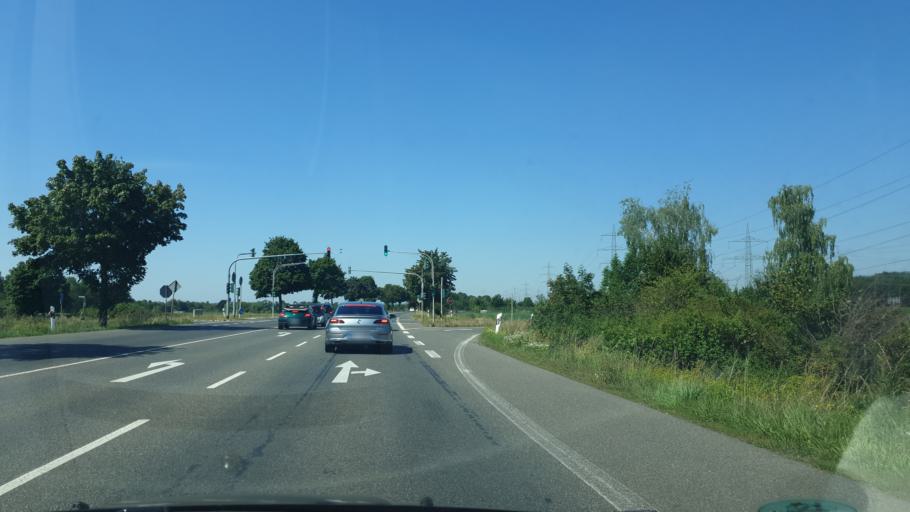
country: DE
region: North Rhine-Westphalia
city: Bornheim
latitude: 50.7682
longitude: 7.0055
